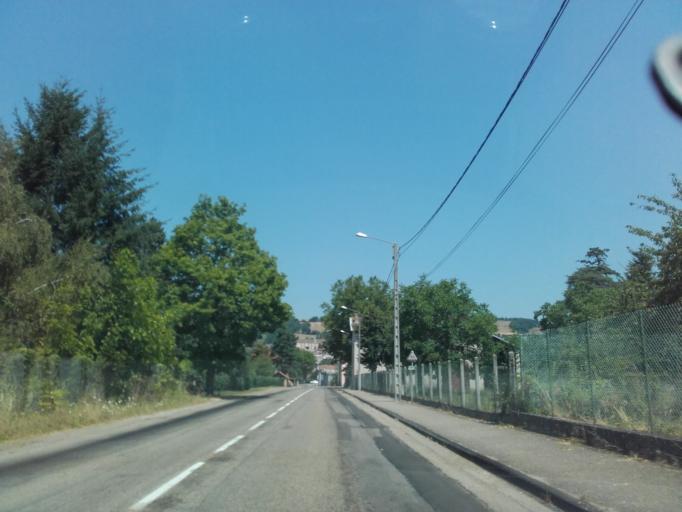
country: FR
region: Rhone-Alpes
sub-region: Departement de l'Isere
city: La Cote-Saint-Andre
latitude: 45.3849
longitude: 5.2627
